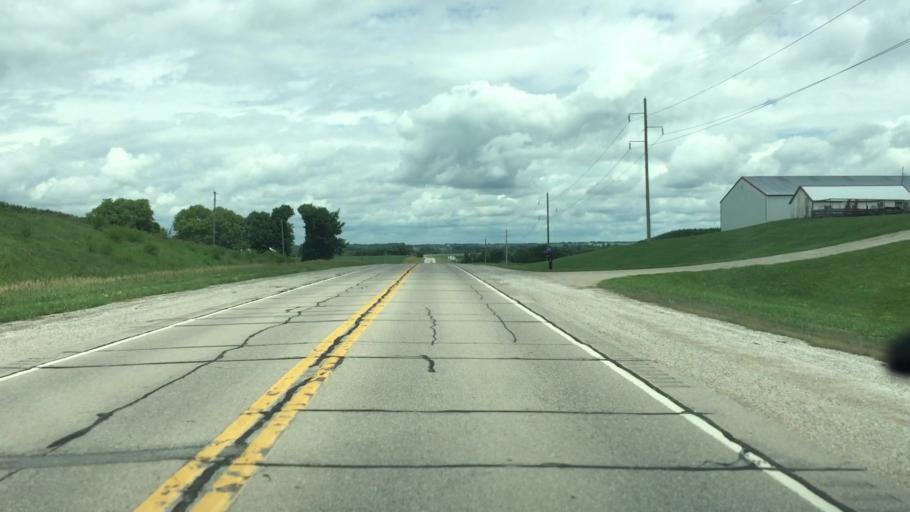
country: US
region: Iowa
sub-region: Jasper County
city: Monroe
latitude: 41.5932
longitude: -93.0968
